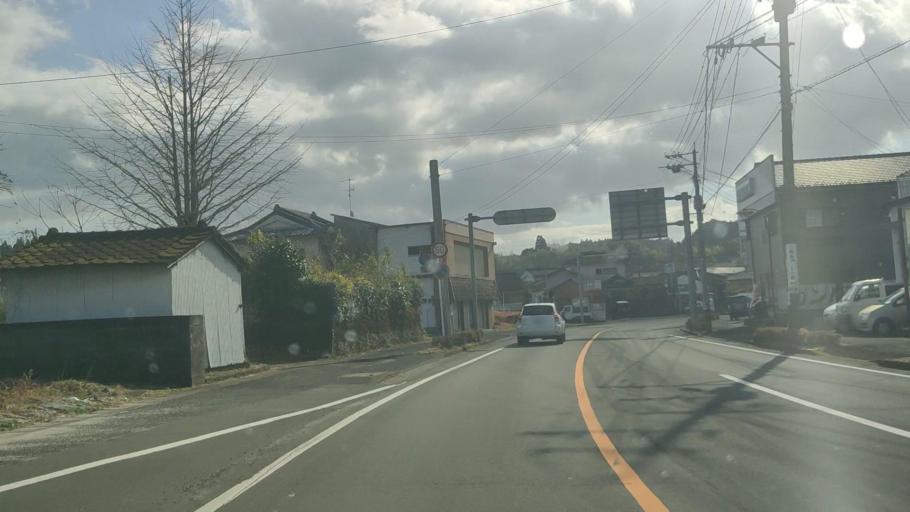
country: JP
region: Kagoshima
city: Okuchi-shinohara
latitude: 31.9517
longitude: 130.7194
